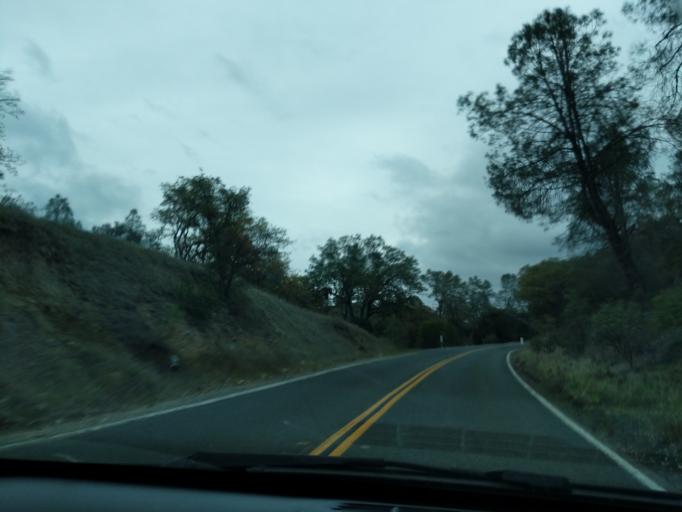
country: US
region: California
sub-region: Monterey County
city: Soledad
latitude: 36.5832
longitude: -121.1930
